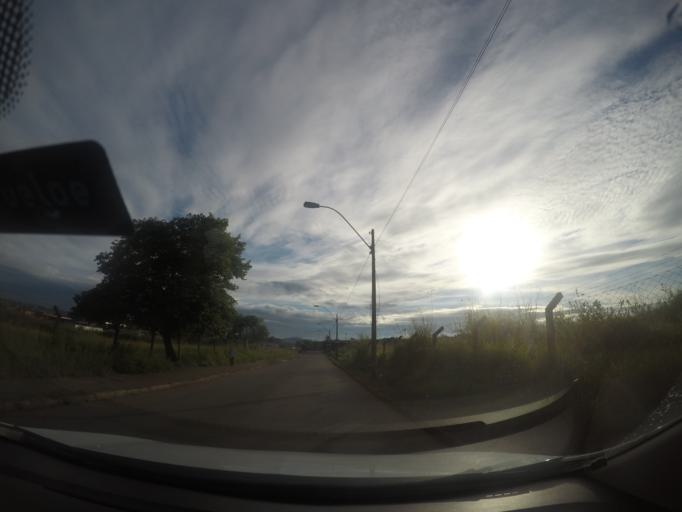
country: BR
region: Goias
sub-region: Goiania
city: Goiania
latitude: -16.6412
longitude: -49.3185
